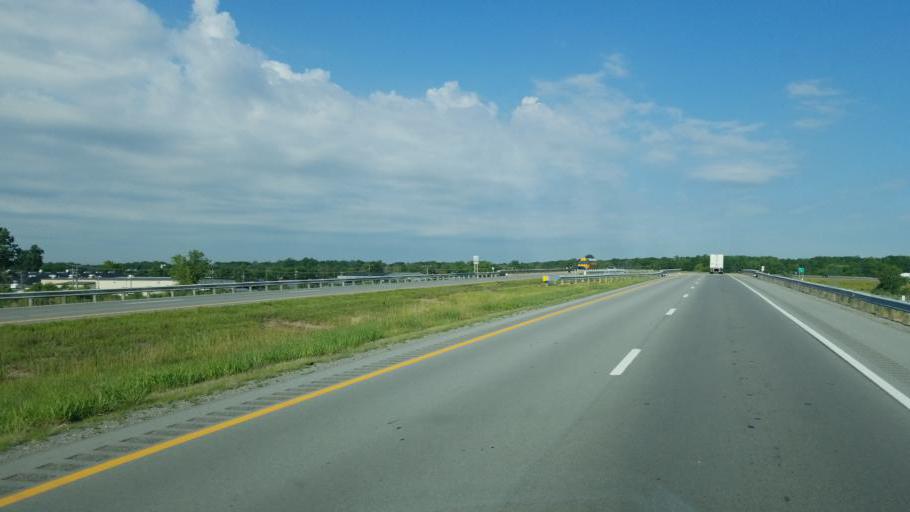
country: US
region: Ohio
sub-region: Hancock County
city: Findlay
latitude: 40.9866
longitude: -83.6406
